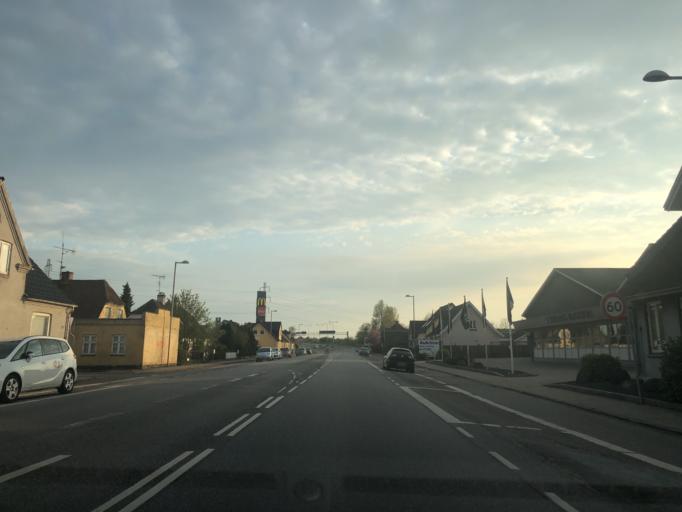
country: DK
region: Zealand
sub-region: Ringsted Kommune
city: Ringsted
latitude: 55.4581
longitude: 11.7944
